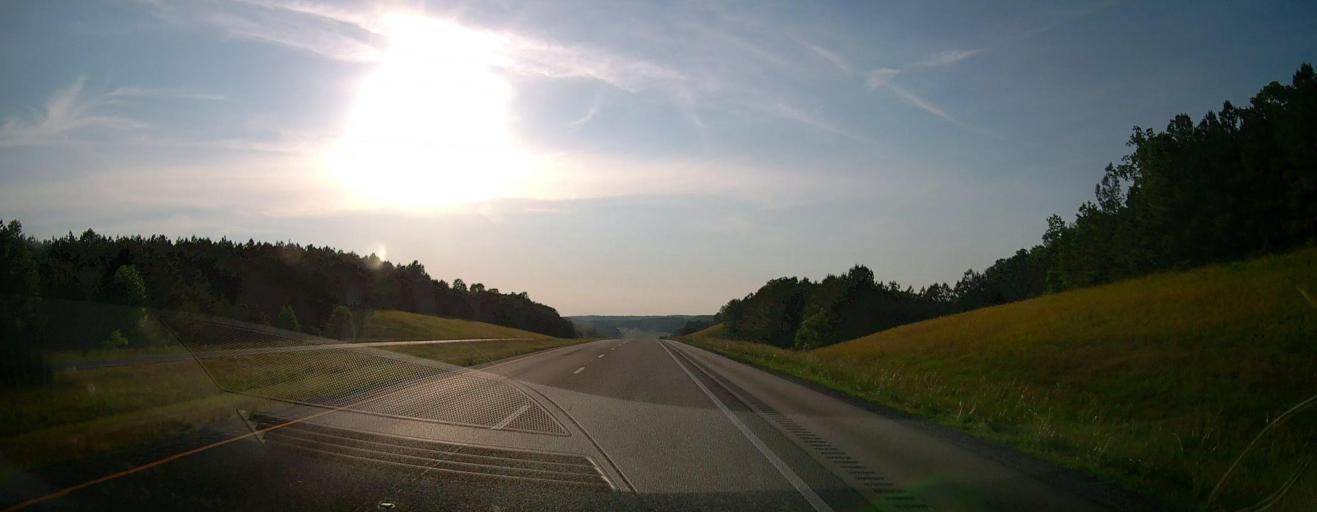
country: US
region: Alabama
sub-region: Marion County
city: Guin
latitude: 34.0326
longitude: -87.8701
